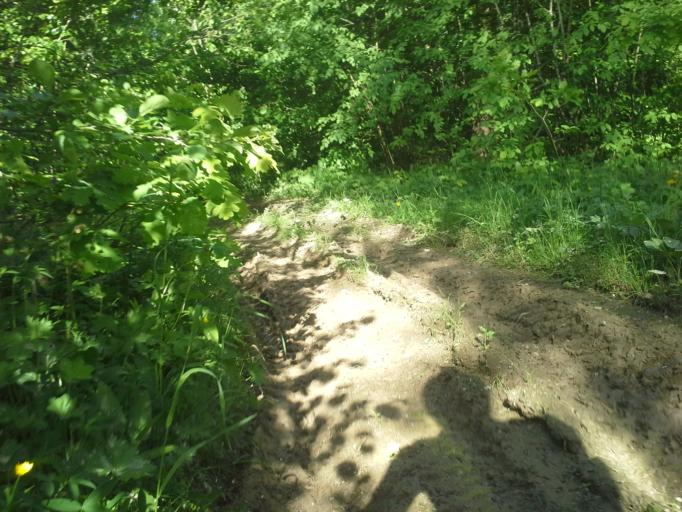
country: RU
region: Moskovskaya
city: Vatutinki
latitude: 55.4644
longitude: 37.4020
